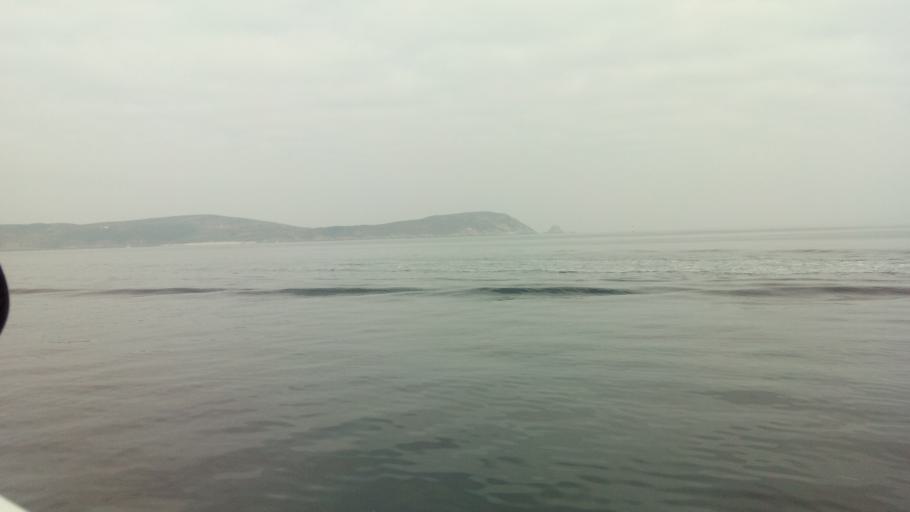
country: ES
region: Galicia
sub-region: Provincia de Pontevedra
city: Sanxenxo
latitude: 42.3794
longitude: -8.8994
